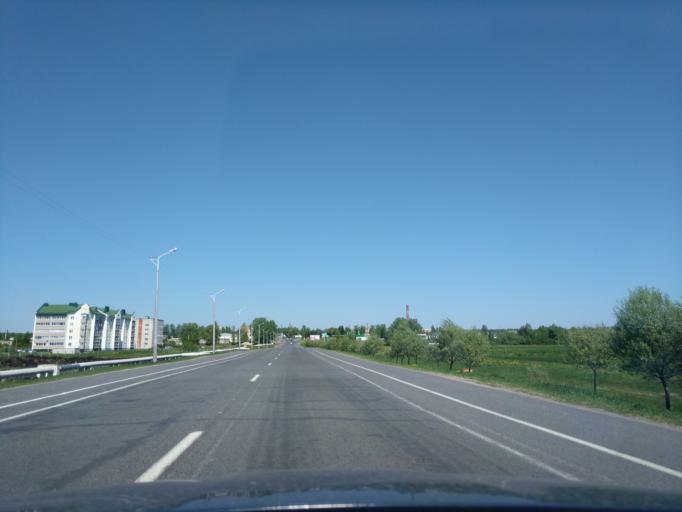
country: BY
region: Minsk
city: Myadzyel
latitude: 54.8783
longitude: 26.9405
